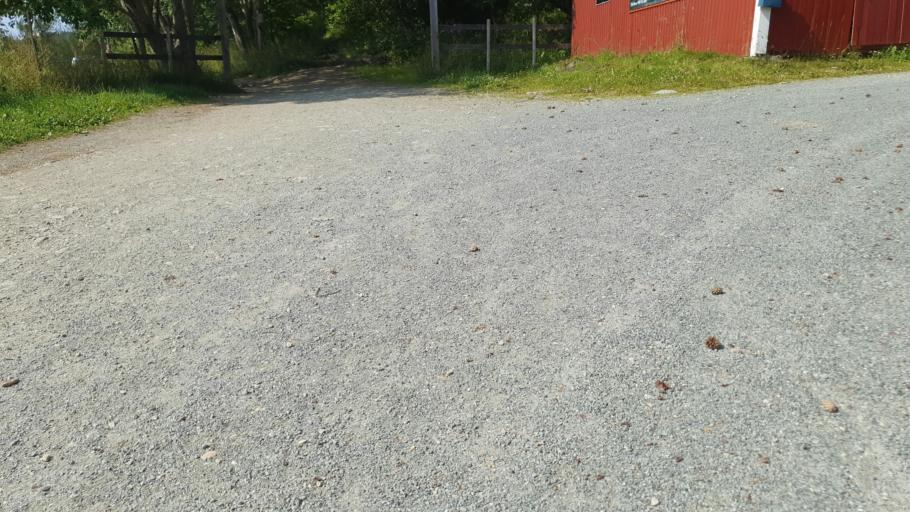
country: NO
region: Sor-Trondelag
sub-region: Trondheim
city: Trondheim
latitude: 63.4192
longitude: 10.3515
